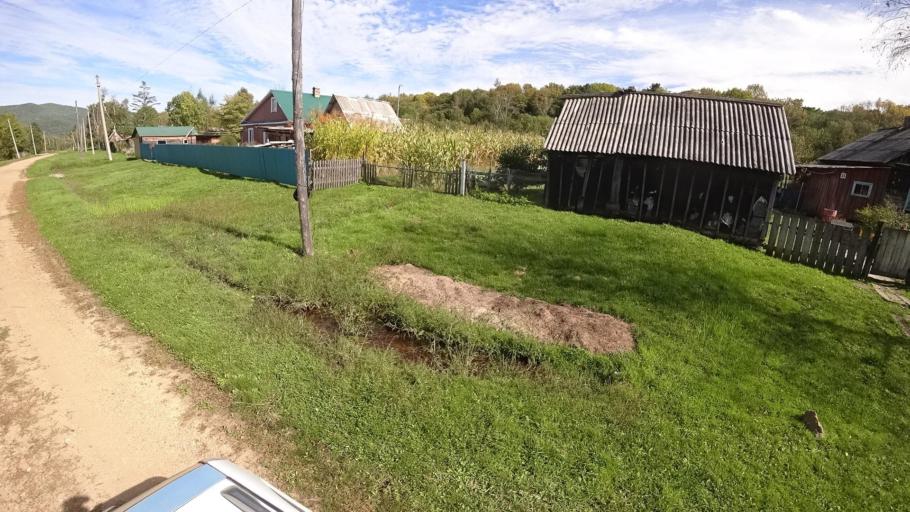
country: RU
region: Primorskiy
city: Yakovlevka
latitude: 44.3864
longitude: 133.5989
